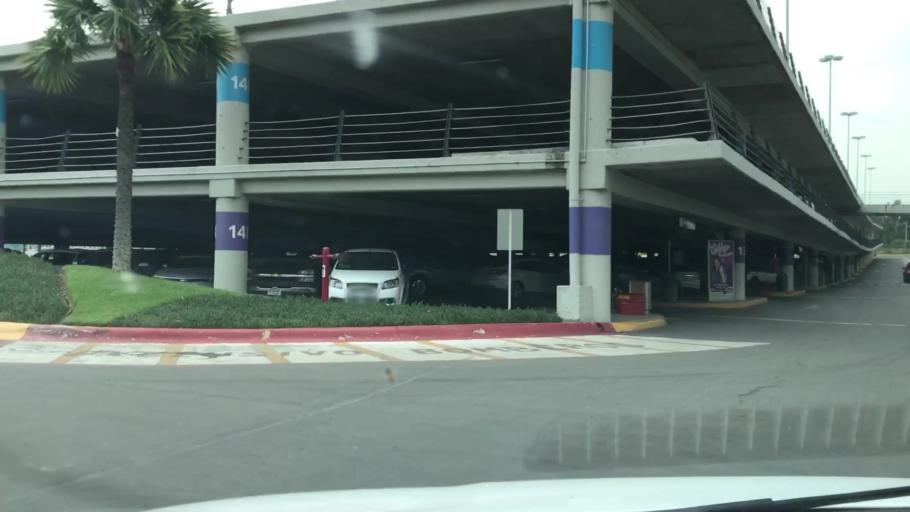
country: MX
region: Jalisco
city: Guadalajara
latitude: 20.6759
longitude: -103.4275
